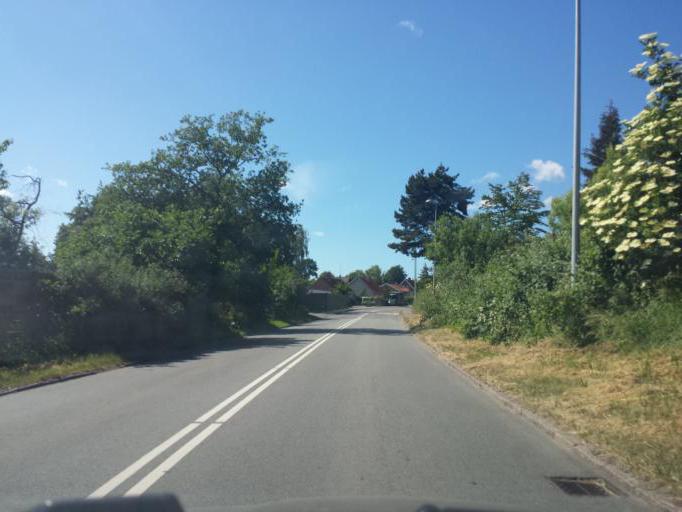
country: DK
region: Capital Region
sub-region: Egedal Kommune
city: Ganlose
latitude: 55.7873
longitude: 12.2695
